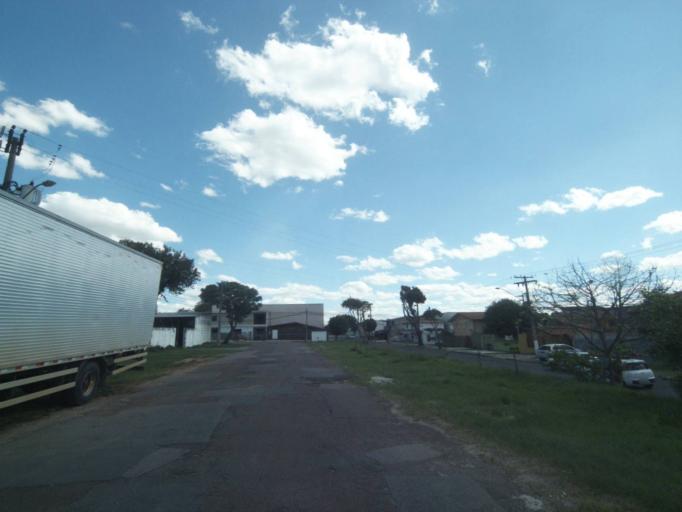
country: BR
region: Parana
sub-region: Curitiba
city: Curitiba
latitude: -25.5026
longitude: -49.3204
